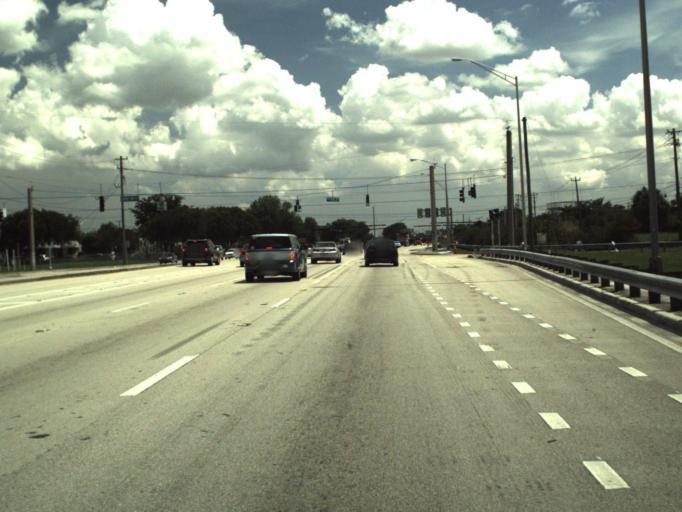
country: US
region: Florida
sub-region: Broward County
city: Cooper City
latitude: 26.0339
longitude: -80.2488
